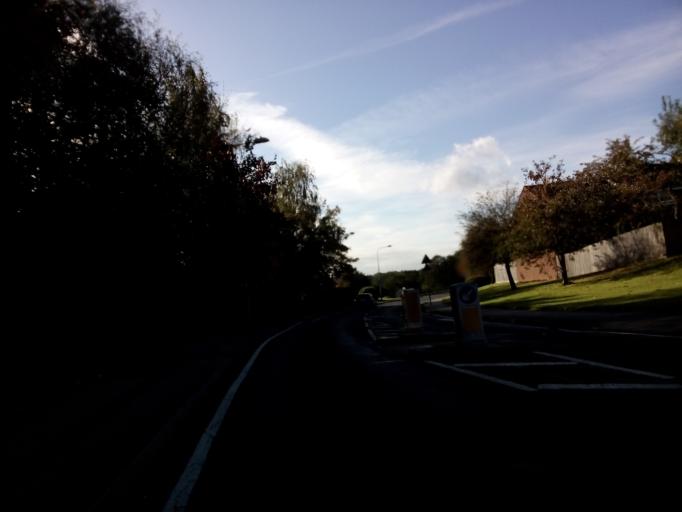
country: GB
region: England
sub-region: Suffolk
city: Ipswich
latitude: 52.0328
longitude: 1.1341
